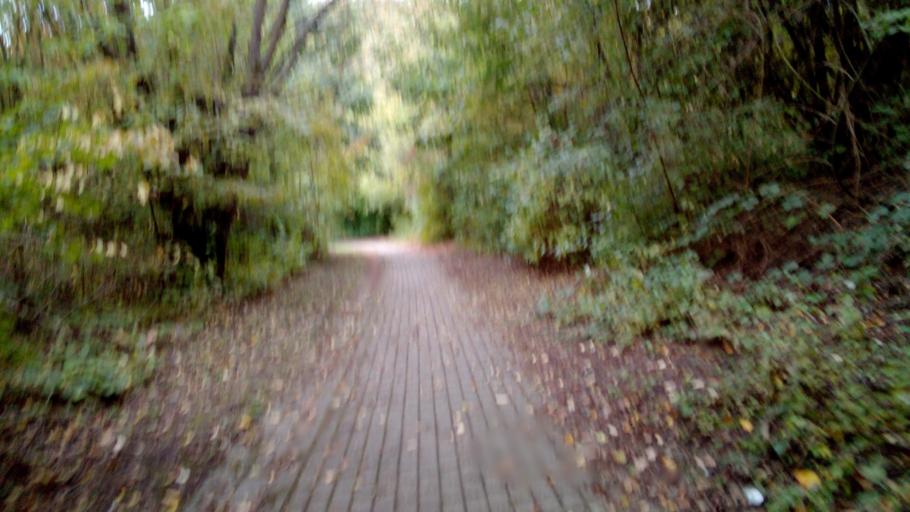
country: DE
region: North Rhine-Westphalia
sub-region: Regierungsbezirk Arnsberg
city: Bochum
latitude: 51.4445
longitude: 7.2514
